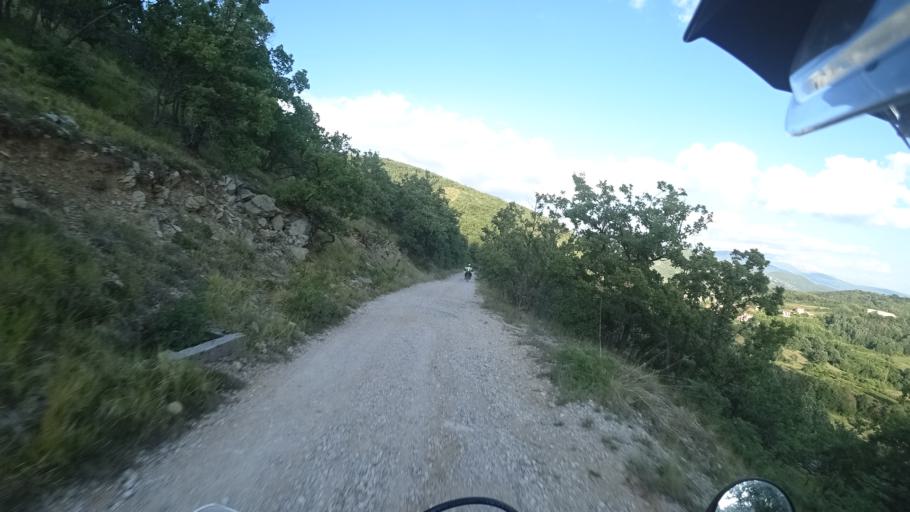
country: HR
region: Sibensko-Kniniska
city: Knin
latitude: 44.1360
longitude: 16.1240
